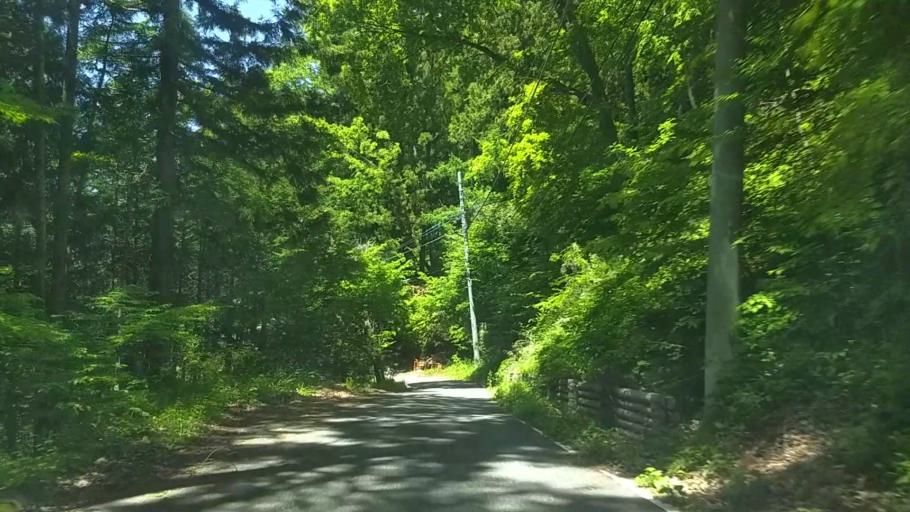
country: JP
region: Yamanashi
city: Nirasaki
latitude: 35.8755
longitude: 138.4327
